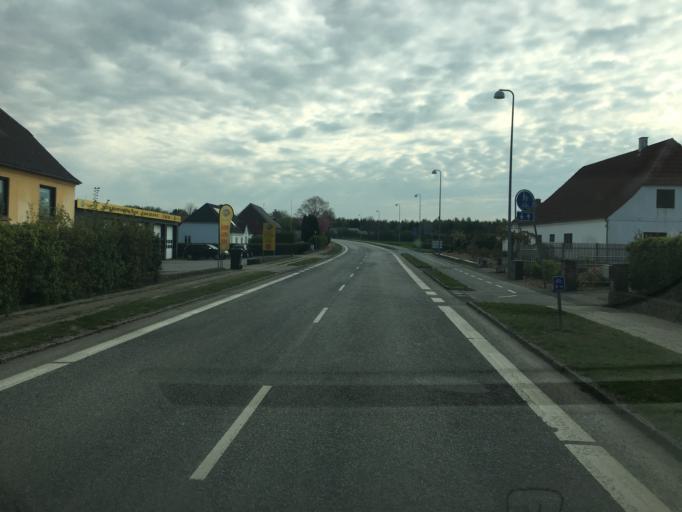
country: DK
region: South Denmark
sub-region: Haderslev Kommune
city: Haderslev
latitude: 55.2083
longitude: 9.4440
